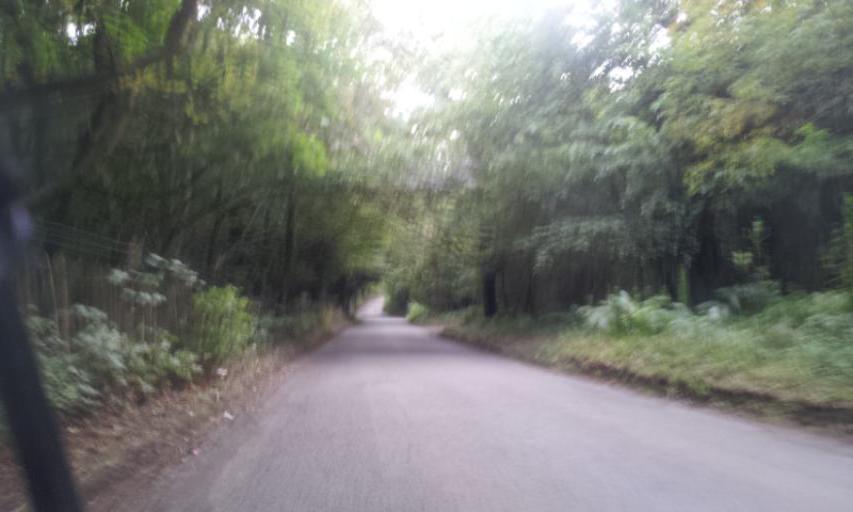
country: GB
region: England
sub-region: Kent
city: Hadlow
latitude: 51.2332
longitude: 0.2969
